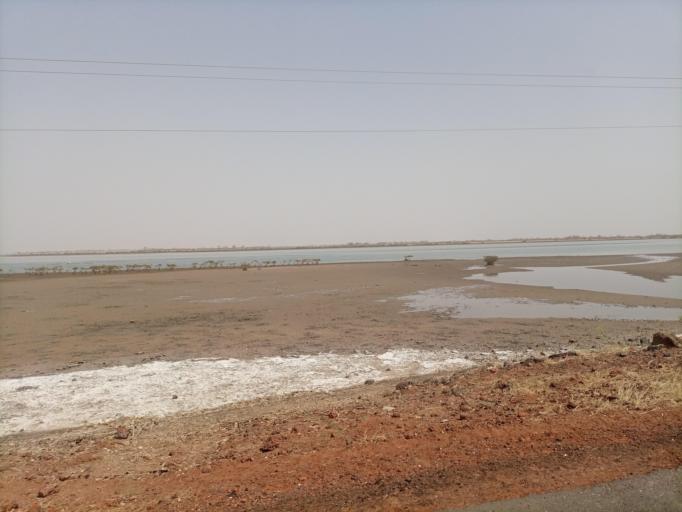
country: SN
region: Fatick
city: Foundiougne
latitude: 14.1904
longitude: -16.4532
